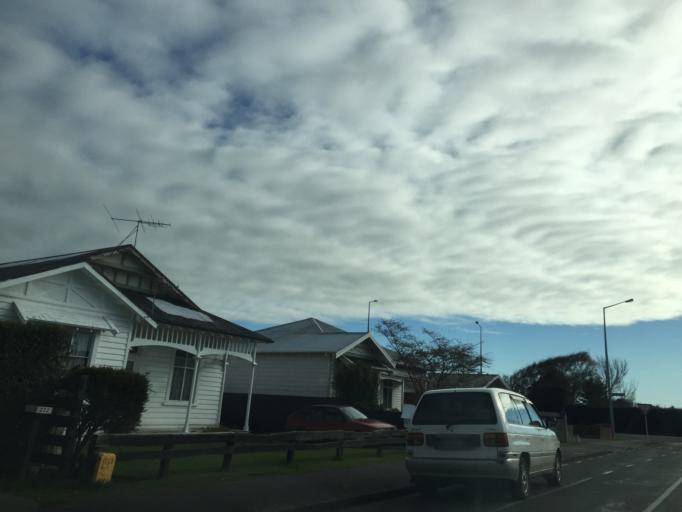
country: NZ
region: Southland
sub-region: Invercargill City
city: Invercargill
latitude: -46.4033
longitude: 168.3670
